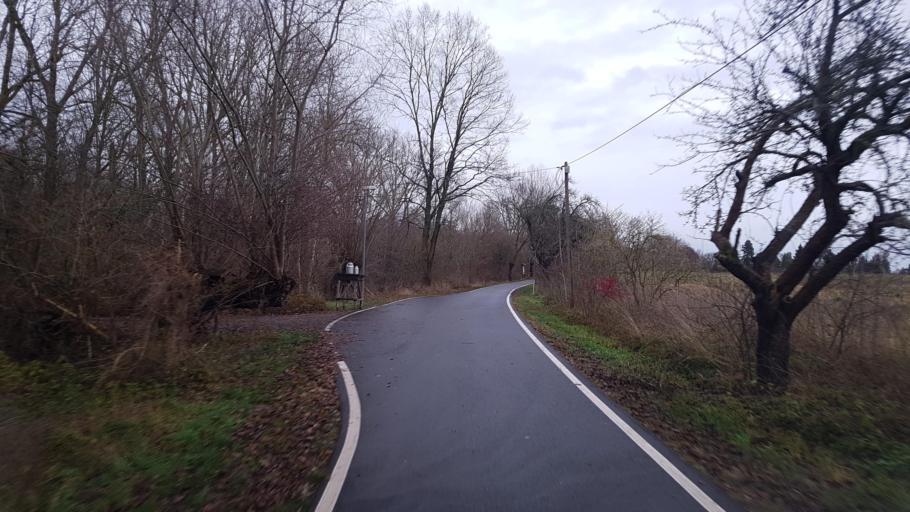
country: DE
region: Brandenburg
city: Tauche
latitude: 52.0899
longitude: 14.1533
